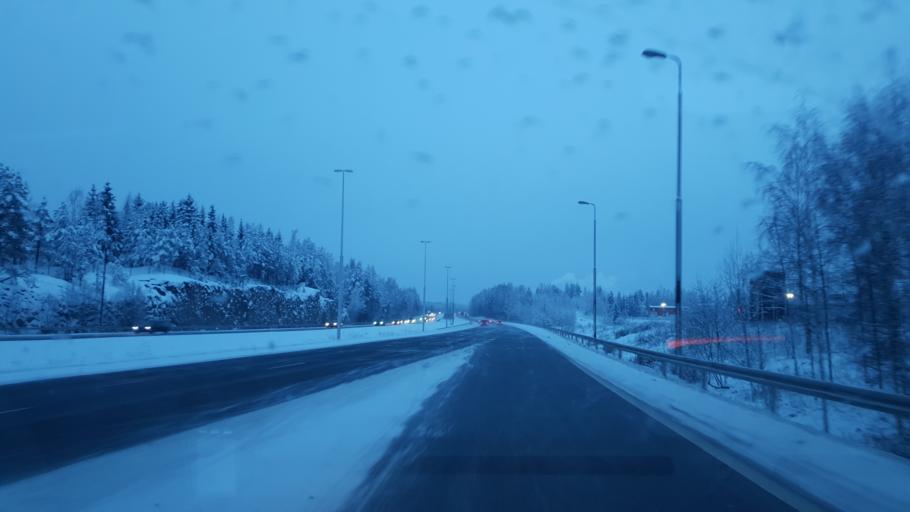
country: FI
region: Uusimaa
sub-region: Helsinki
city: Kerava
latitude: 60.3836
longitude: 25.1173
